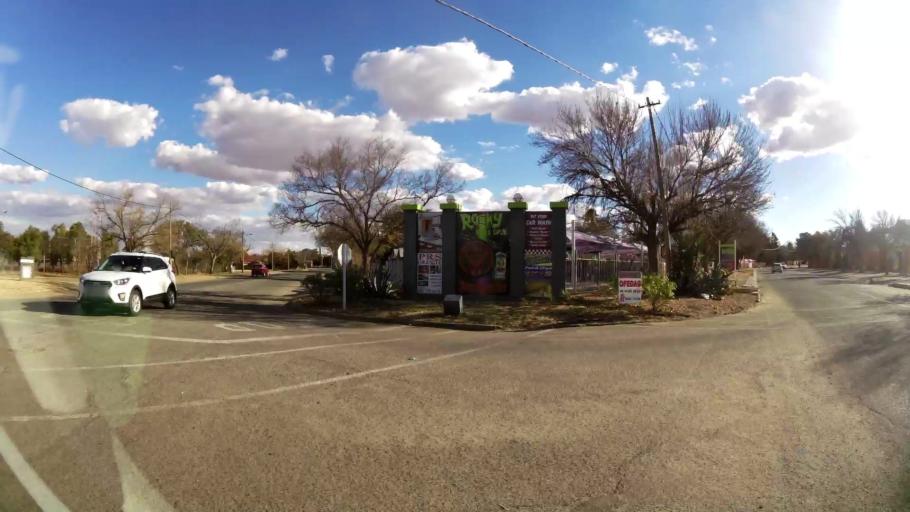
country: ZA
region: North-West
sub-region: Dr Kenneth Kaunda District Municipality
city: Klerksdorp
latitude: -26.8441
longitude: 26.6639
